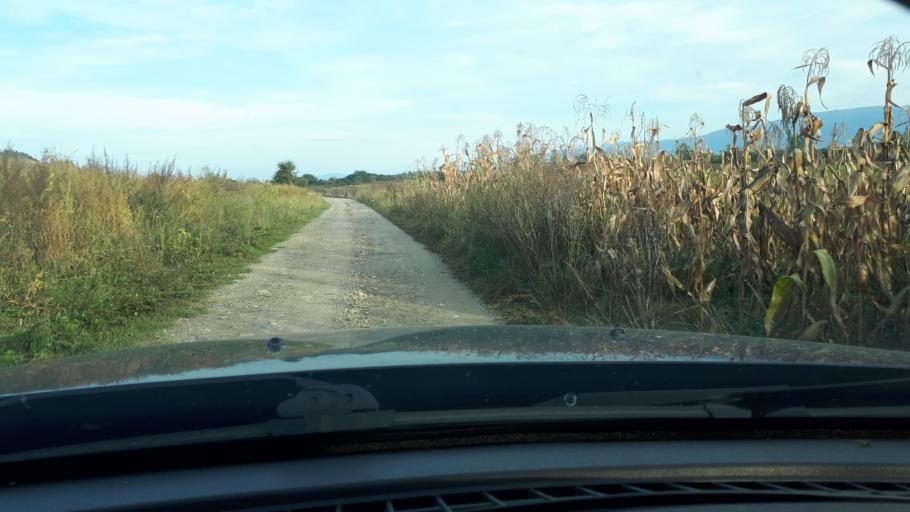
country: RO
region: Brasov
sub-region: Comuna Vistea de Jos
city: Vistea de Jos
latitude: 45.8200
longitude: 24.7744
